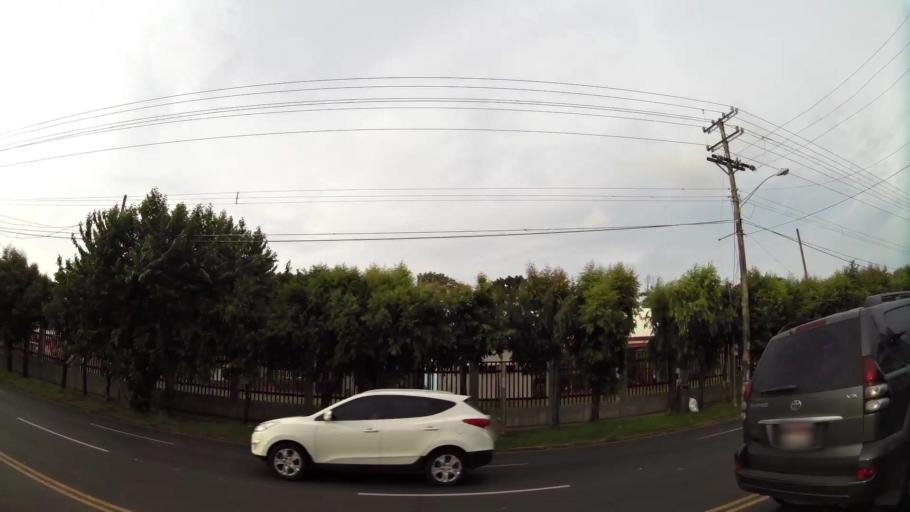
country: PA
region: Panama
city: Panama
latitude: 8.9970
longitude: -79.5081
